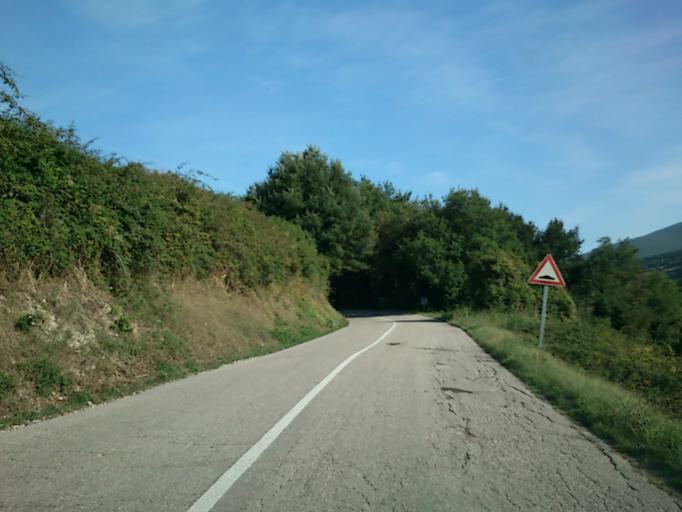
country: IT
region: The Marches
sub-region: Provincia di Pesaro e Urbino
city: Canavaccio
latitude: 43.6837
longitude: 12.7284
